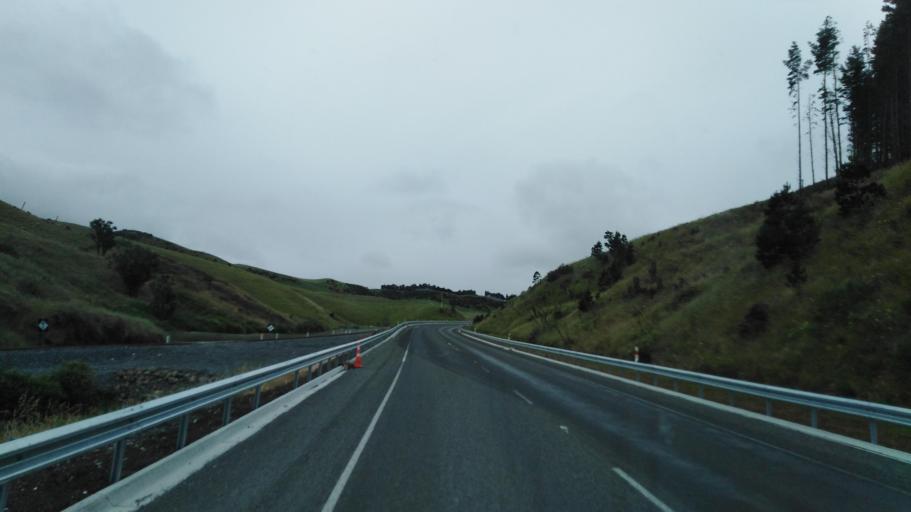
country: NZ
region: Marlborough
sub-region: Marlborough District
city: Blenheim
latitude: -41.8937
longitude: 174.1165
